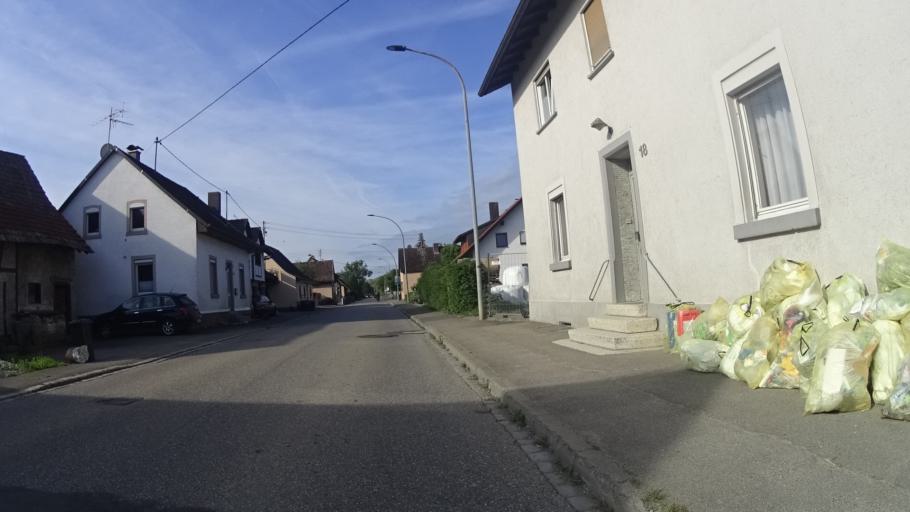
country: DE
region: Baden-Wuerttemberg
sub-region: Freiburg Region
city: Neuenburg am Rhein
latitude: 47.8421
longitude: 7.5771
